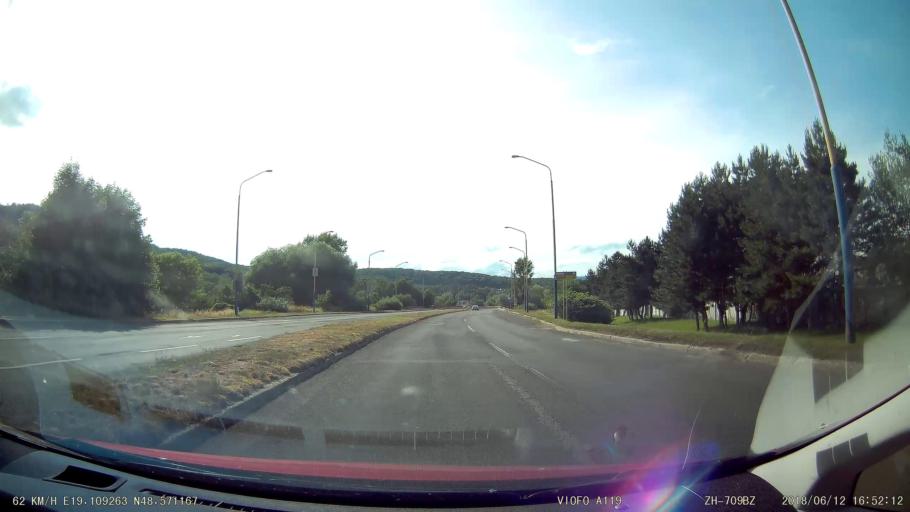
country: SK
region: Banskobystricky
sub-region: Okres Banska Bystrica
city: Zvolen
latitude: 48.5717
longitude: 19.1089
